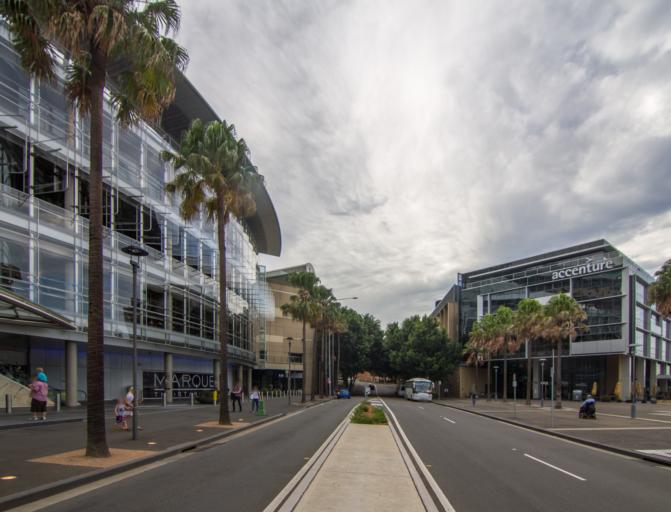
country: AU
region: New South Wales
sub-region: Leichhardt
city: Balmain East
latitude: -33.8676
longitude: 151.1960
